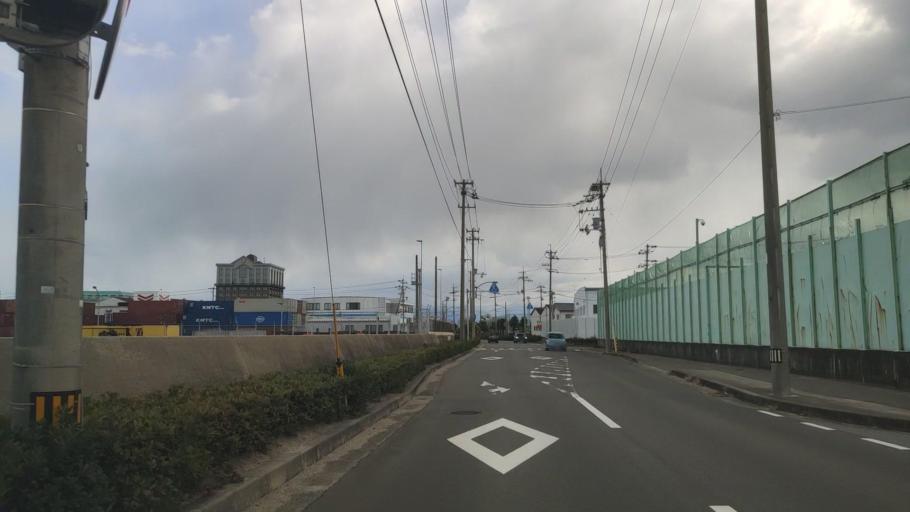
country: JP
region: Ehime
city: Saijo
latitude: 34.0505
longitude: 133.0246
